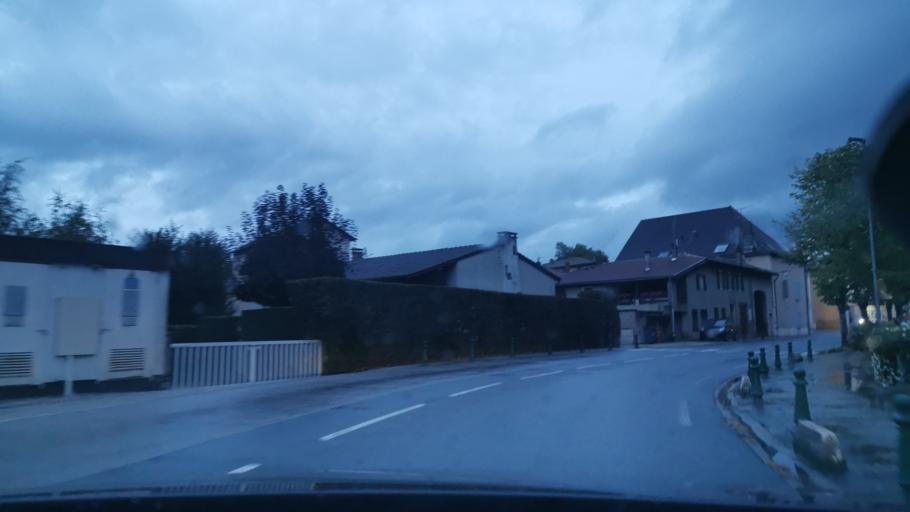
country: FR
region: Rhone-Alpes
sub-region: Departement de l'Ain
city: Pont-de-Veyle
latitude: 46.2654
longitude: 4.8878
